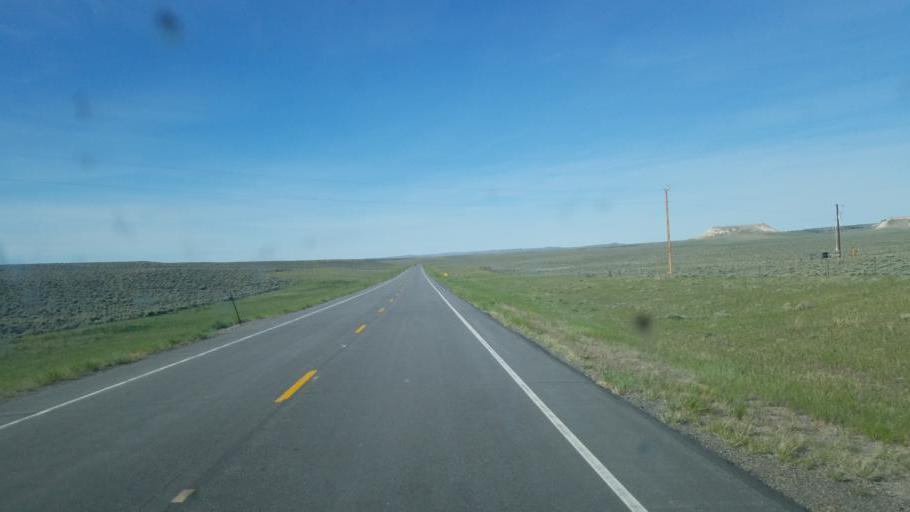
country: US
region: Wyoming
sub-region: Fremont County
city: Riverton
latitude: 42.6572
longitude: -108.1874
